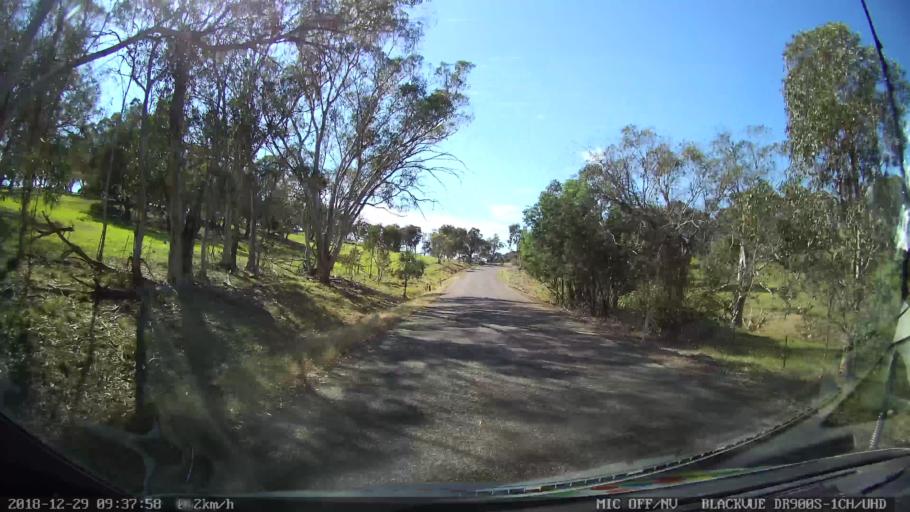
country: AU
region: New South Wales
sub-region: Upper Lachlan Shire
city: Crookwell
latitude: -34.6424
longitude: 149.3746
